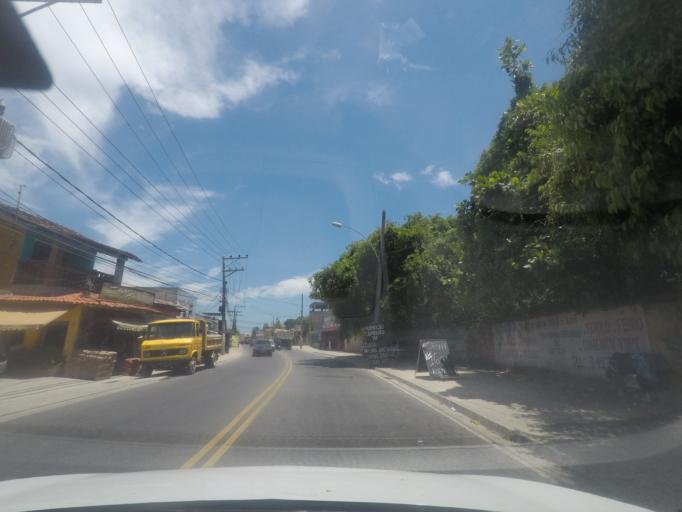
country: BR
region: Rio de Janeiro
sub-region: Itaguai
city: Itaguai
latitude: -22.9276
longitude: -43.6908
